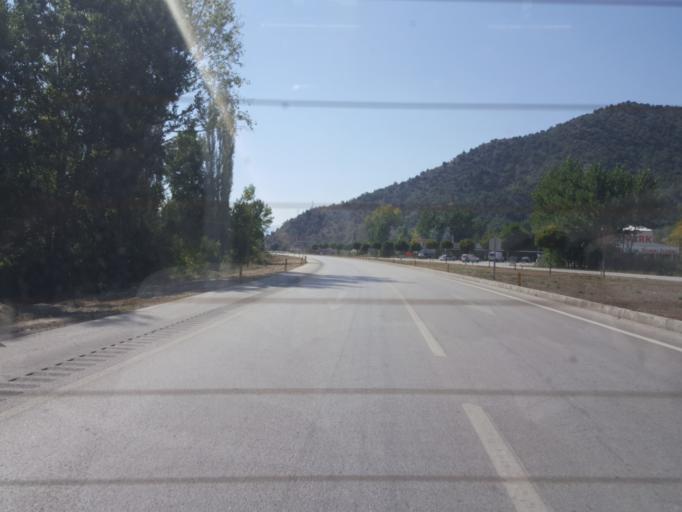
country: TR
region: Corum
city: Osmancik
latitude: 40.9758
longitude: 34.9147
